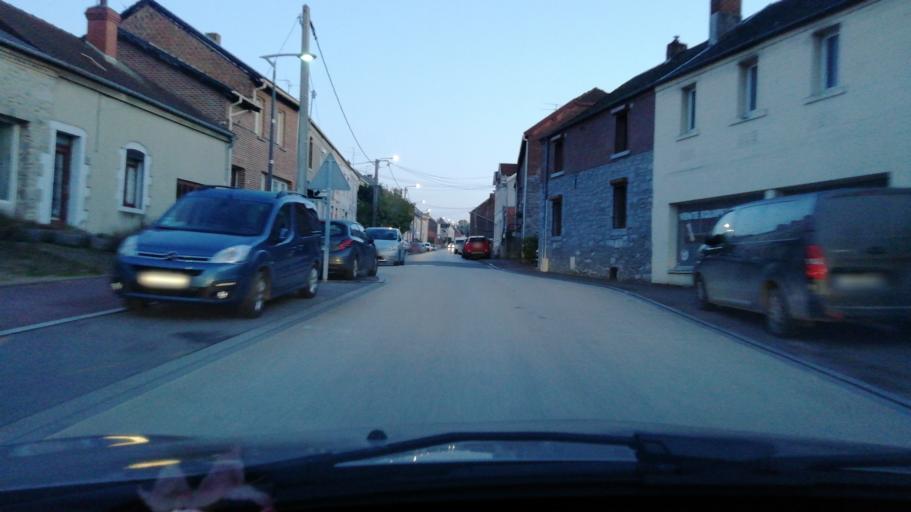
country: FR
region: Nord-Pas-de-Calais
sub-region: Departement du Nord
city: Marpent
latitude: 50.2917
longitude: 4.0811
